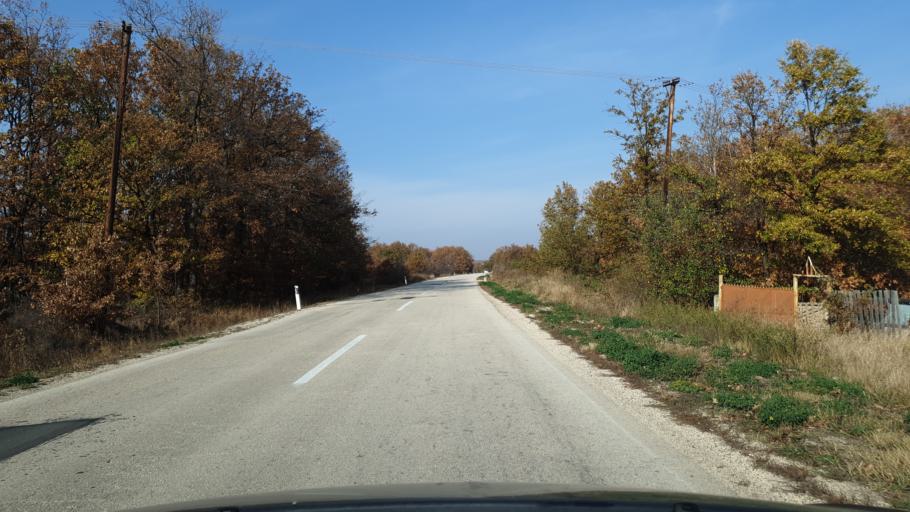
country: RS
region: Central Serbia
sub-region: Borski Okrug
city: Bor
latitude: 43.9938
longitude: 22.0724
